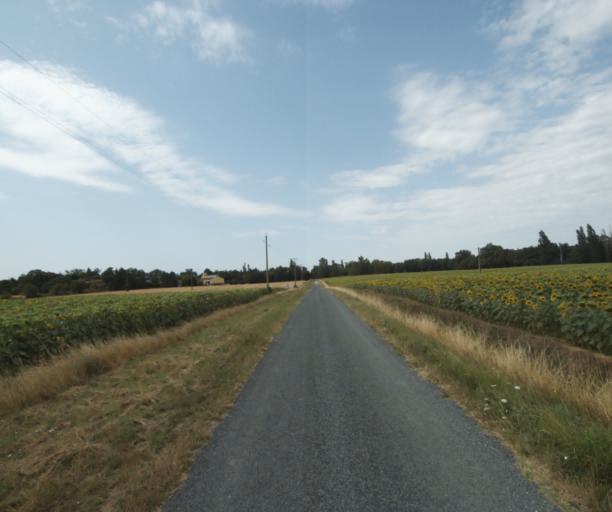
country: FR
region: Midi-Pyrenees
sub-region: Departement de la Haute-Garonne
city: Saint-Felix-Lauragais
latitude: 43.4302
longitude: 1.9013
